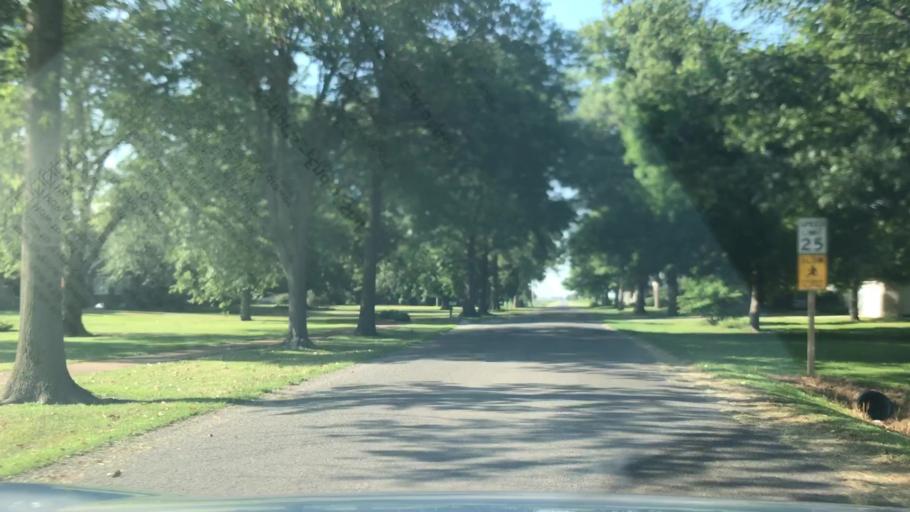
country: US
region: Illinois
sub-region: Washington County
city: Okawville
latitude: 38.3928
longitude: -89.4865
